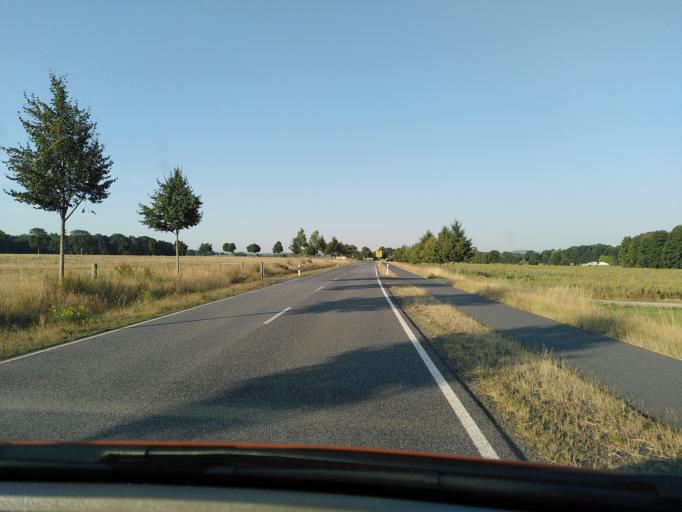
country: DE
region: Saxony
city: Horka
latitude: 51.2832
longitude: 14.2479
